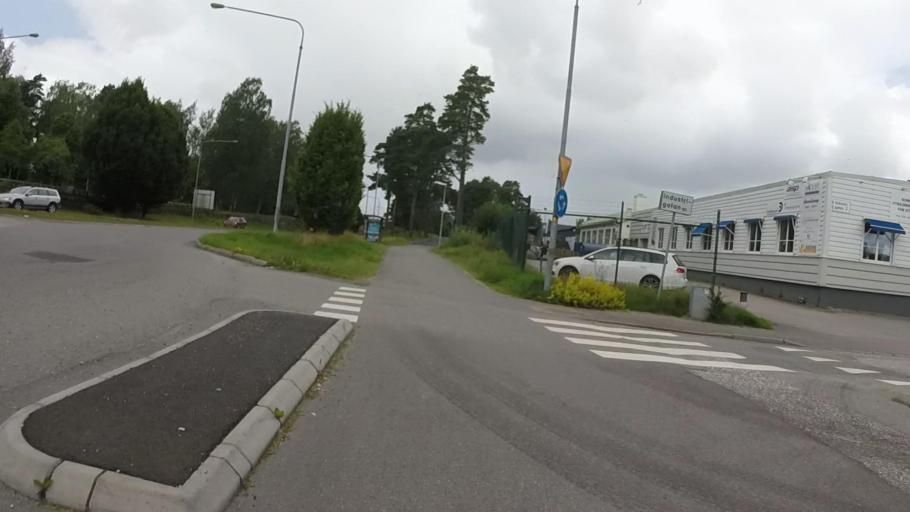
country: SE
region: Vaestra Goetaland
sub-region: Trollhattan
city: Trollhattan
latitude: 58.2787
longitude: 12.3096
